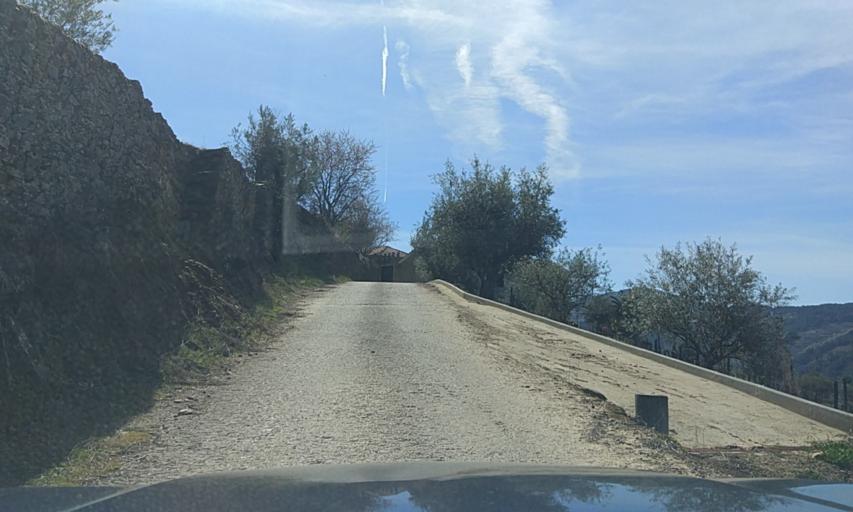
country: PT
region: Vila Real
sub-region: Sabrosa
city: Sabrosa
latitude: 41.3019
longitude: -7.5464
